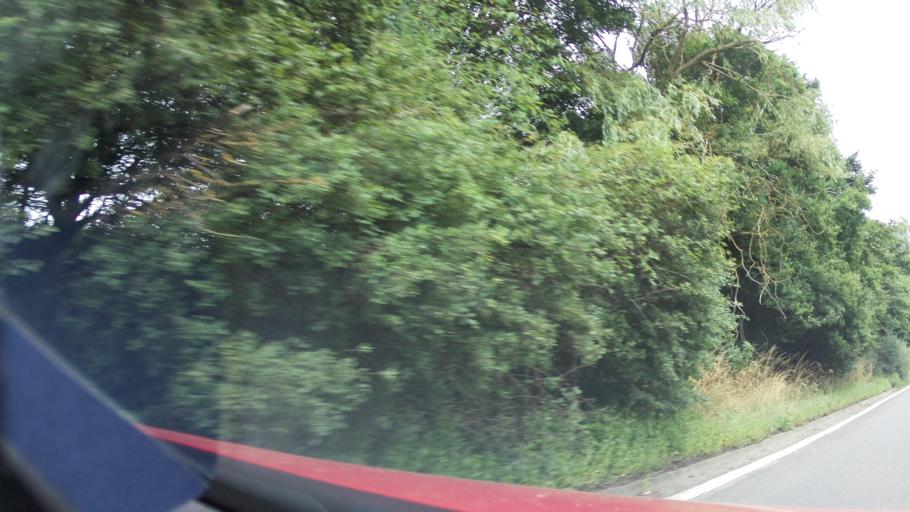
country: GB
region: England
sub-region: Northamptonshire
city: Corby
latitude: 52.4787
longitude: -0.7372
